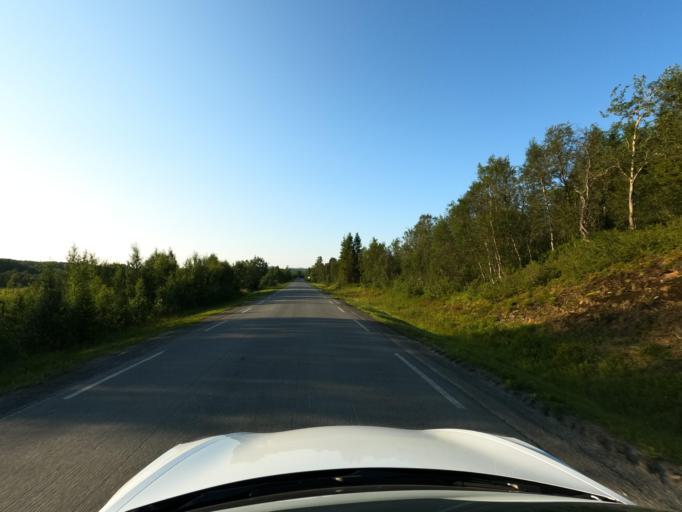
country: NO
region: Troms
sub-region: Skanland
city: Evenskjer
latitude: 68.4811
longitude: 16.7112
